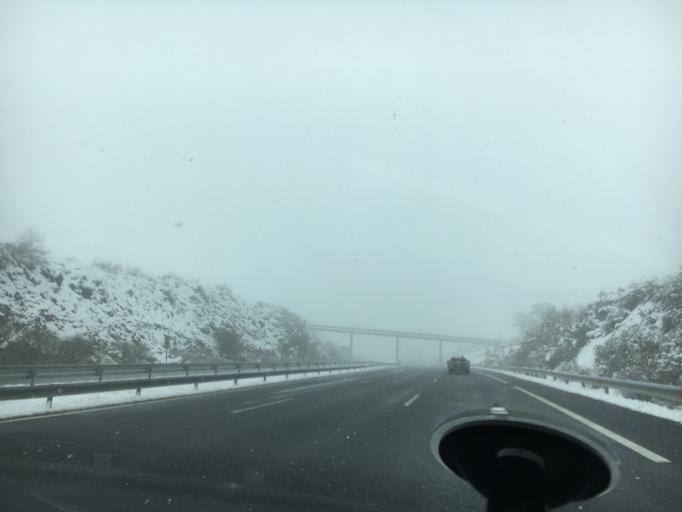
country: ES
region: Castille and Leon
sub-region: Provincia de Zamora
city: Pias
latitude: 42.0561
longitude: -7.1107
